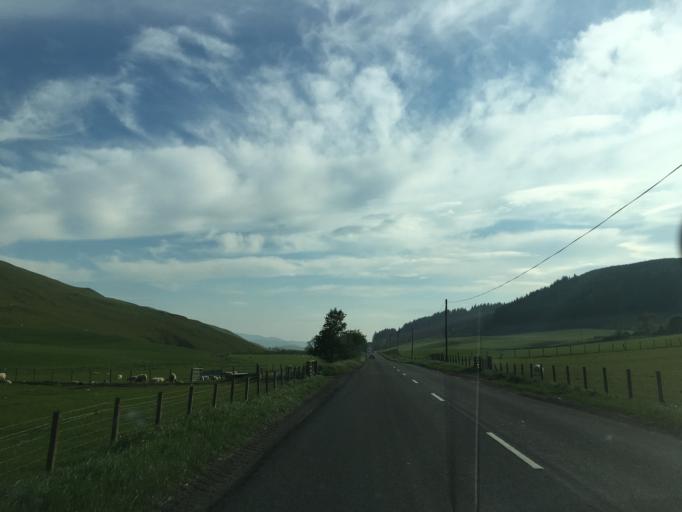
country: GB
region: Scotland
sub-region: The Scottish Borders
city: West Linton
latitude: 55.6697
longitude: -3.4194
